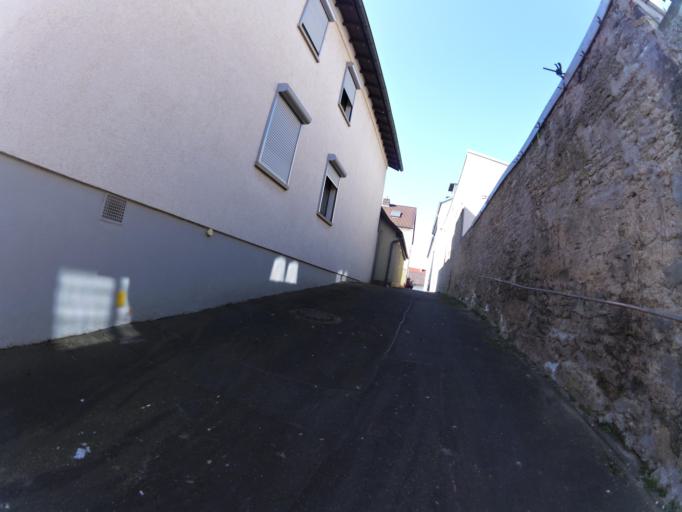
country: DE
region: Bavaria
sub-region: Regierungsbezirk Unterfranken
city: Unterpleichfeld
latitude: 49.8684
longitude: 10.0466
